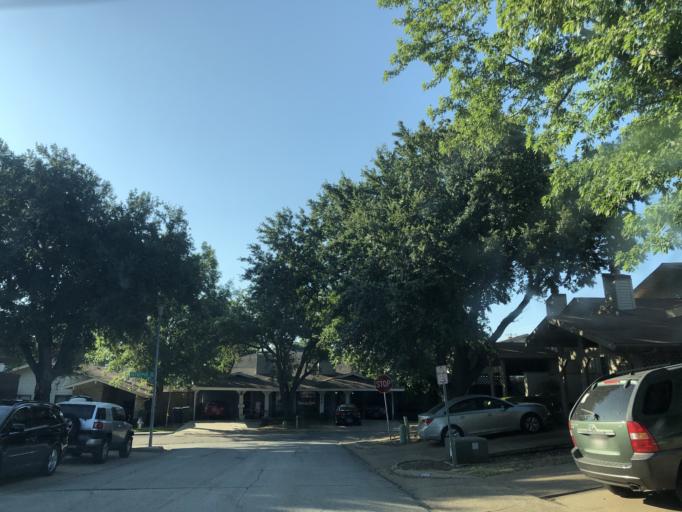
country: US
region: Texas
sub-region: Dallas County
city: Garland
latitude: 32.8591
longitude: -96.6392
